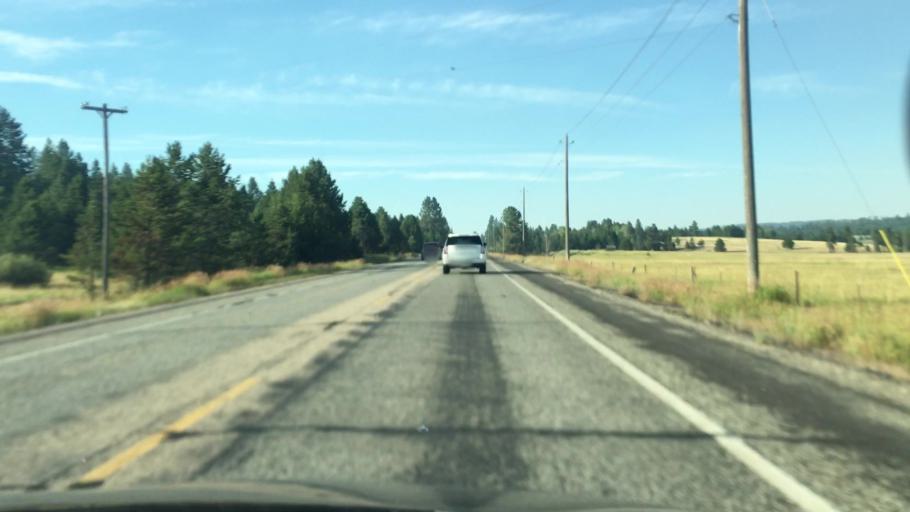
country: US
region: Idaho
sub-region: Valley County
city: Cascade
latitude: 44.3593
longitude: -116.0215
